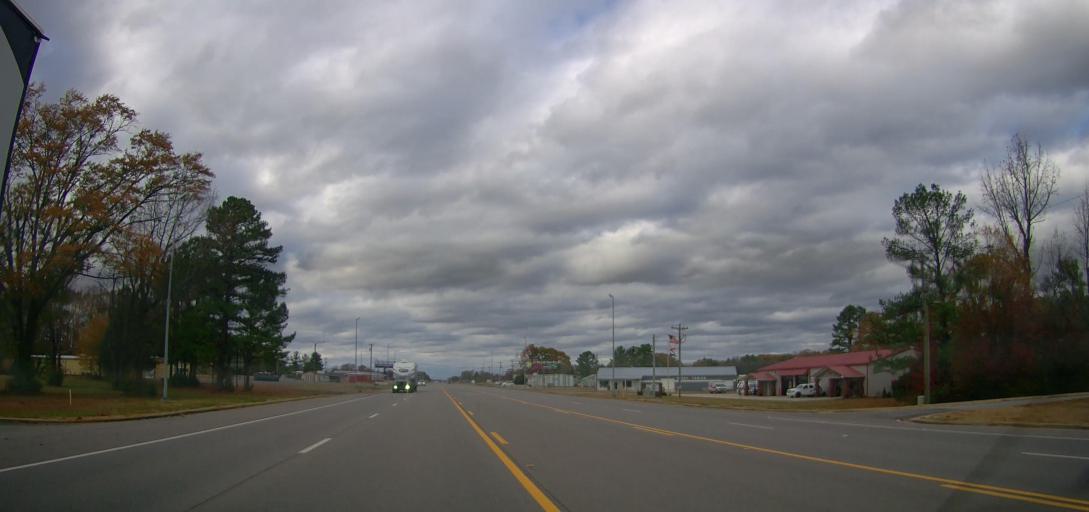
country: US
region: Alabama
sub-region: Lawrence County
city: Moulton
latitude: 34.5067
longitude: -87.2870
